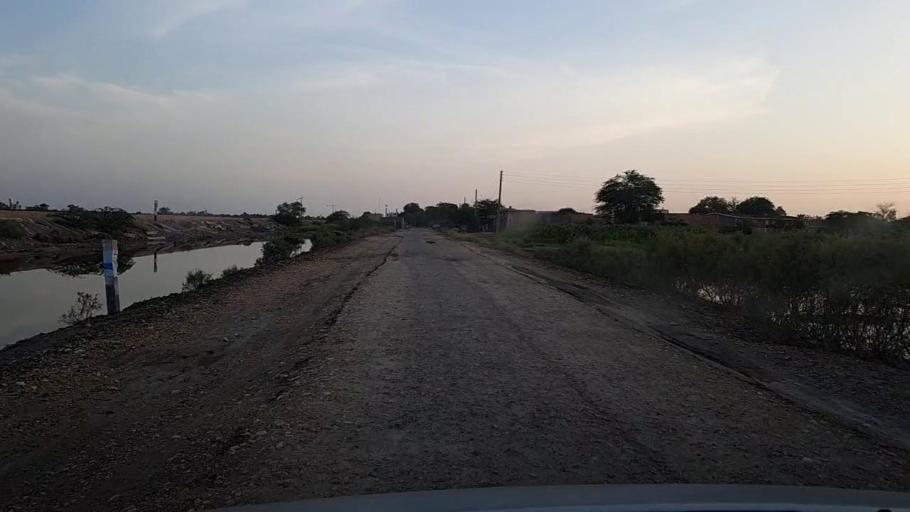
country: PK
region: Sindh
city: Karaundi
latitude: 27.0471
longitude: 68.3842
